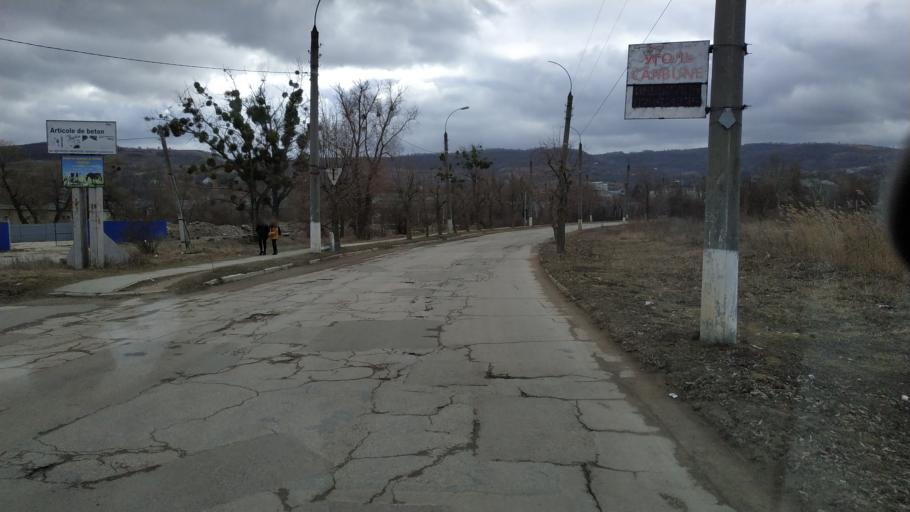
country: MD
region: Calarasi
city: Calarasi
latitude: 47.2463
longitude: 28.3166
